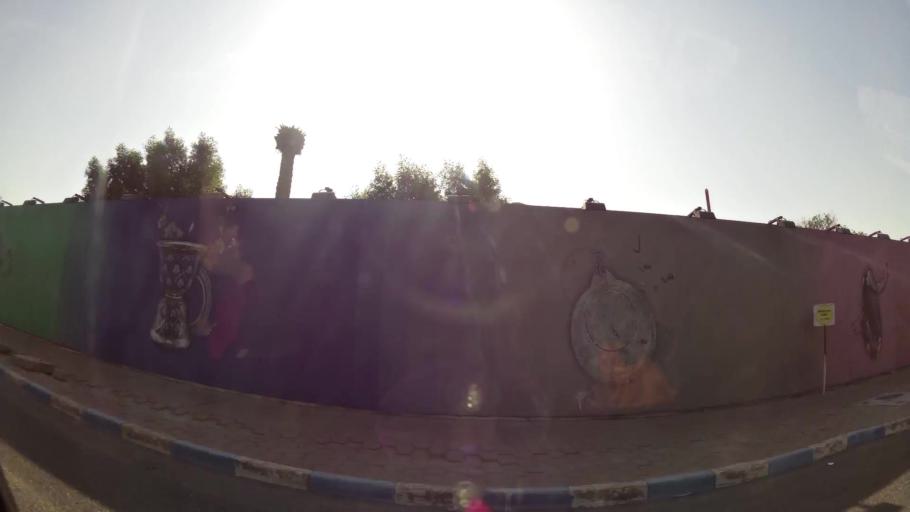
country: KW
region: Al Asimah
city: Kuwait City
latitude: 29.3740
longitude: 47.9660
